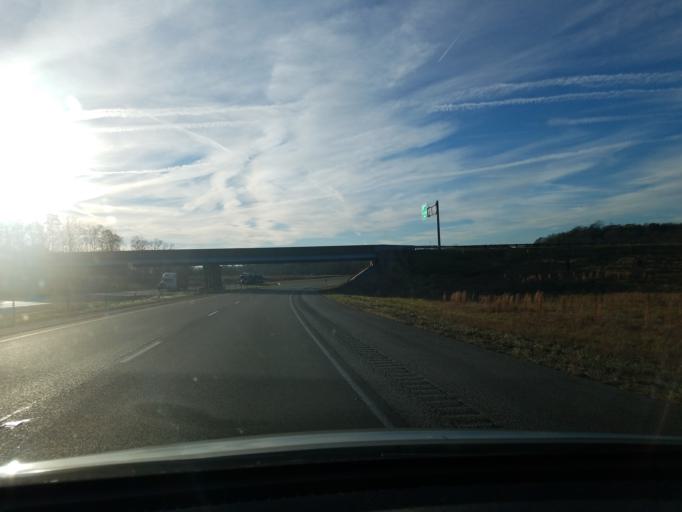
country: US
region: Indiana
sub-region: Crawford County
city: English
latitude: 38.2264
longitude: -86.5905
